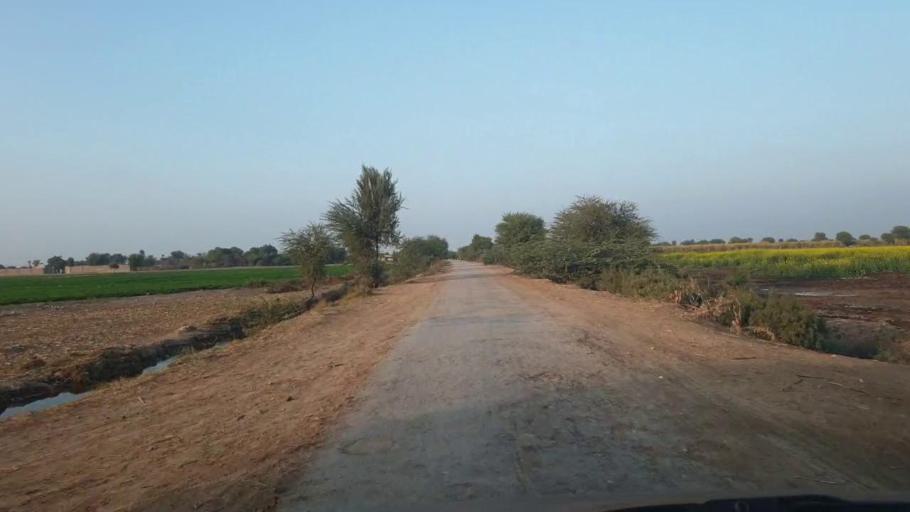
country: PK
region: Sindh
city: Berani
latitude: 25.8336
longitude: 68.7445
